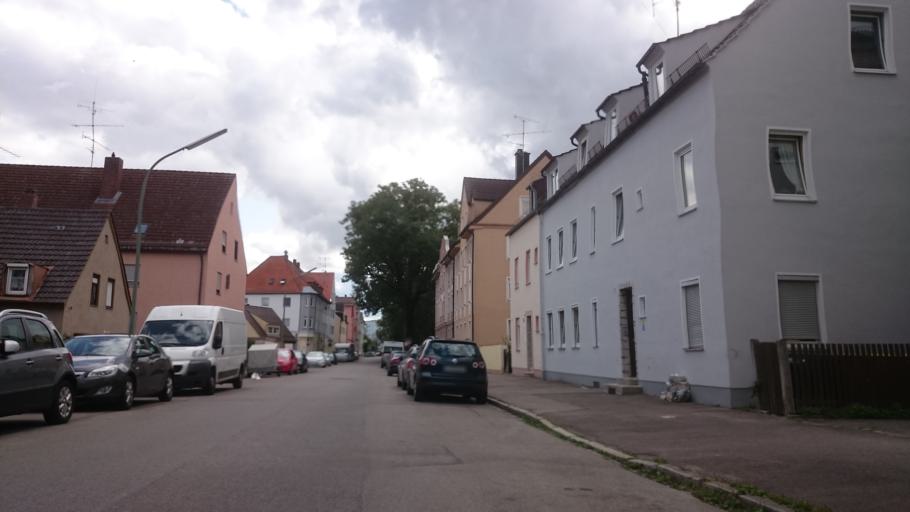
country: DE
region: Bavaria
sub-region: Swabia
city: Augsburg
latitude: 48.3757
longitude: 10.9226
